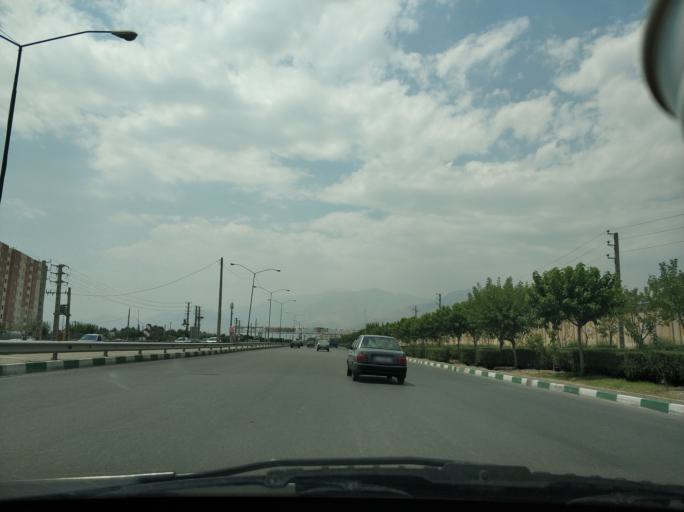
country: IR
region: Tehran
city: Tajrish
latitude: 35.7598
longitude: 51.5727
